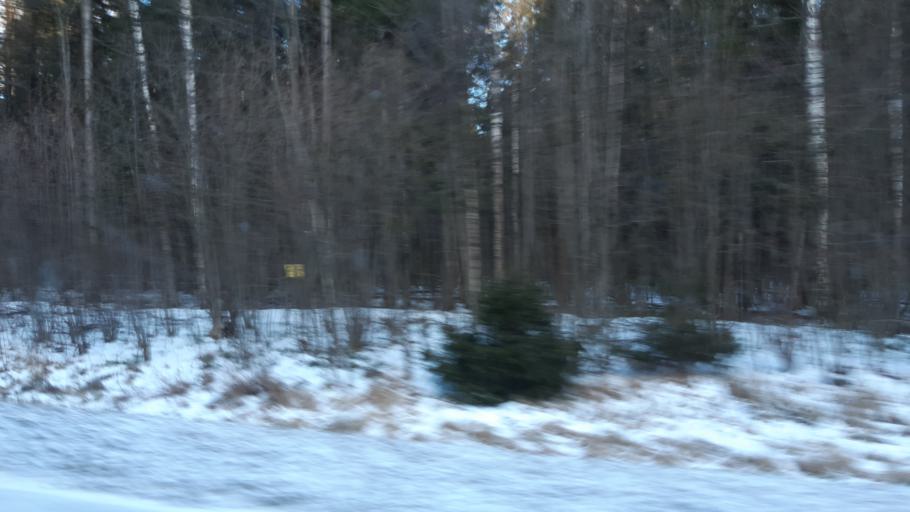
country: RU
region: Vladimir
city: Arsaki
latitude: 56.2737
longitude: 38.4141
